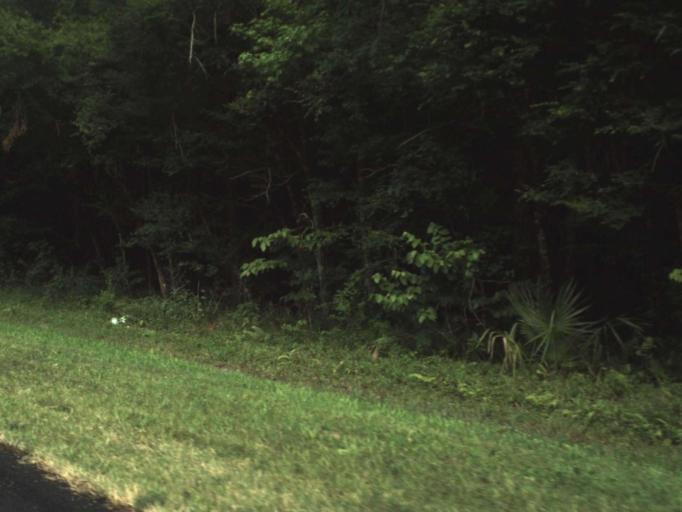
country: US
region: Florida
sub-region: Seminole County
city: Winter Springs
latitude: 28.7193
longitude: -81.3207
